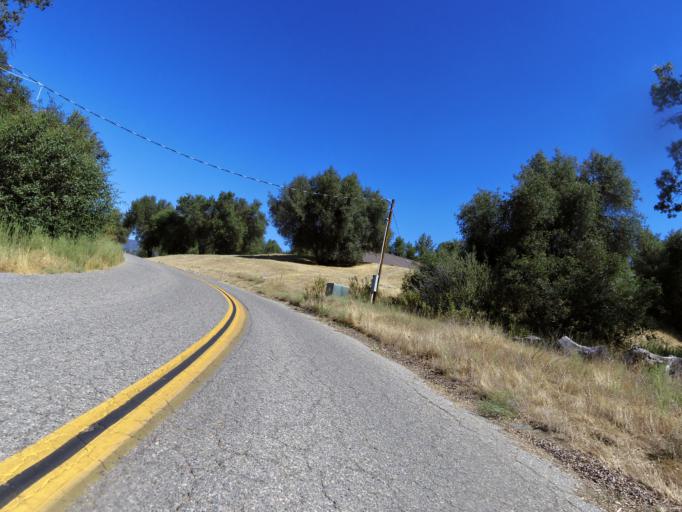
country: US
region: California
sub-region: Madera County
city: Ahwahnee
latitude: 37.3651
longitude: -119.6987
